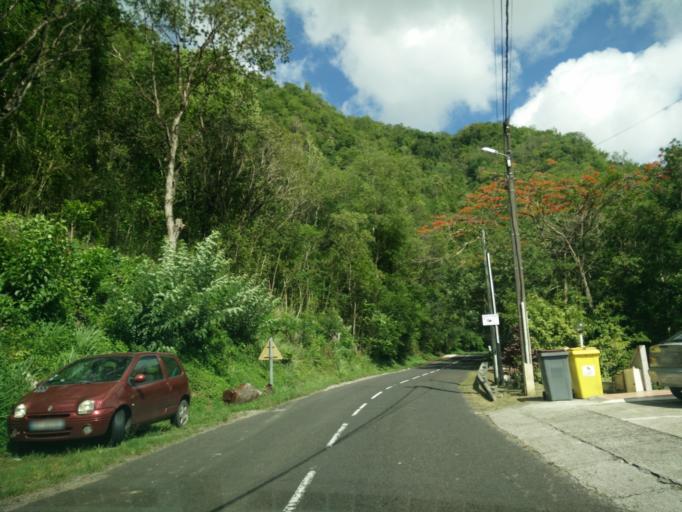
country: MQ
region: Martinique
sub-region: Martinique
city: Les Trois-Ilets
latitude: 14.5173
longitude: -61.0744
